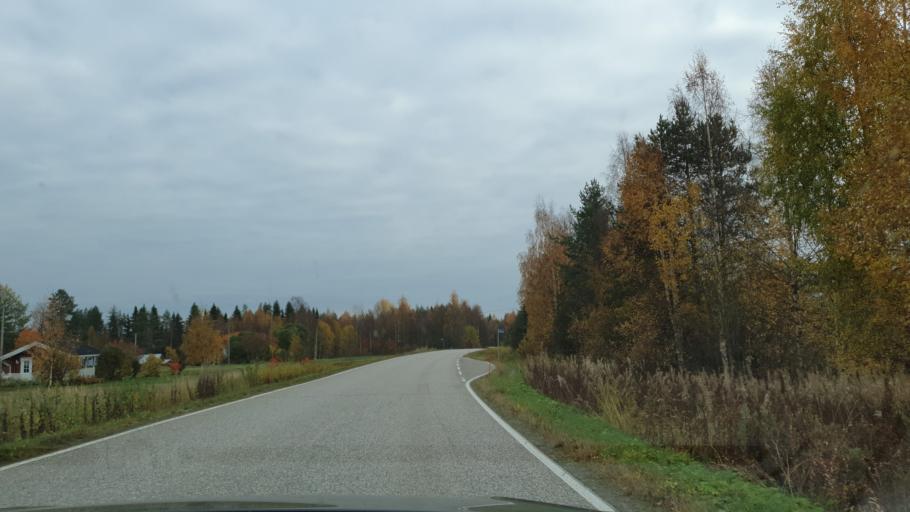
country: FI
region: Kainuu
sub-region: Kajaani
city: Ristijaervi
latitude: 64.4674
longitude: 28.3052
